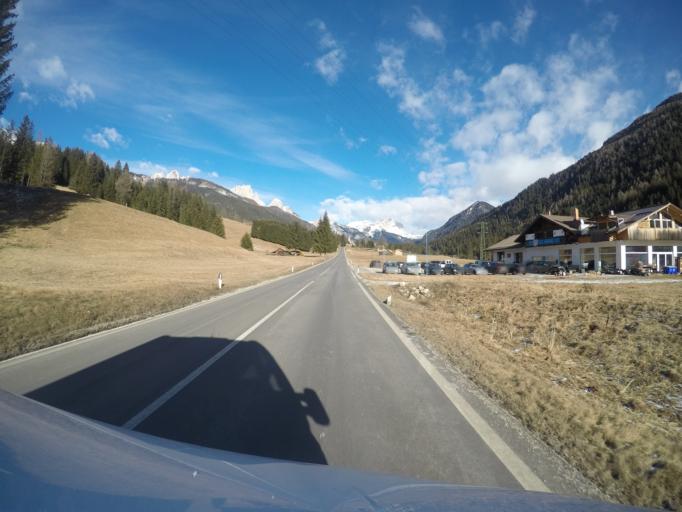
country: IT
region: Trentino-Alto Adige
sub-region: Provincia di Trento
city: Vigo di Fassa
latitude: 46.4093
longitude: 11.6766
